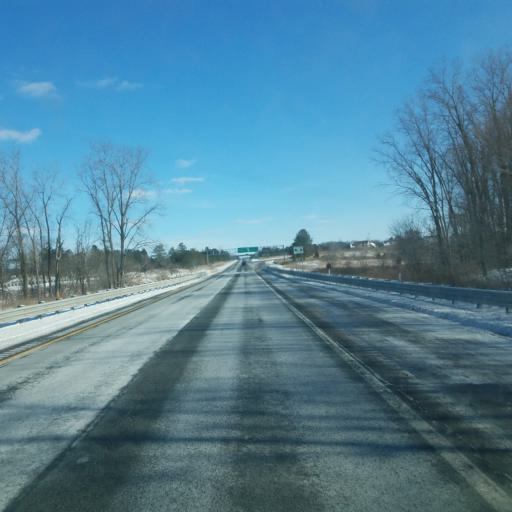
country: US
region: Michigan
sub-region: Ingham County
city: Williamston
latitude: 42.6654
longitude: -84.2909
